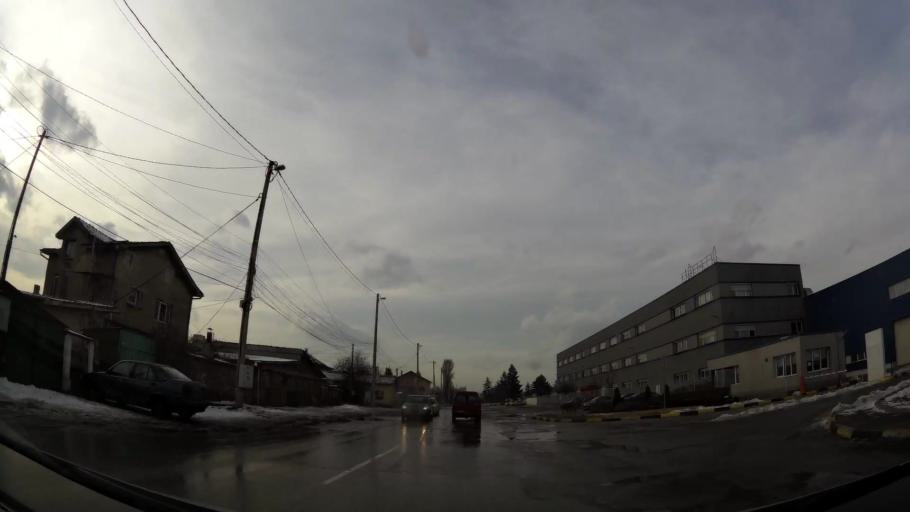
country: BG
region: Sofia-Capital
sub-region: Stolichna Obshtina
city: Sofia
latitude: 42.6935
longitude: 23.3792
